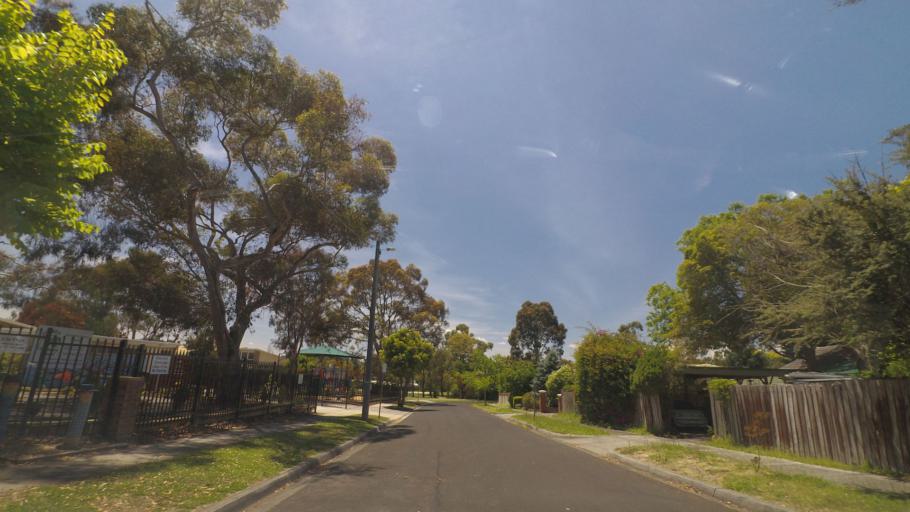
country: AU
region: Victoria
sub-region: Maroondah
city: Croydon South
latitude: -37.8104
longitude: 145.2860
